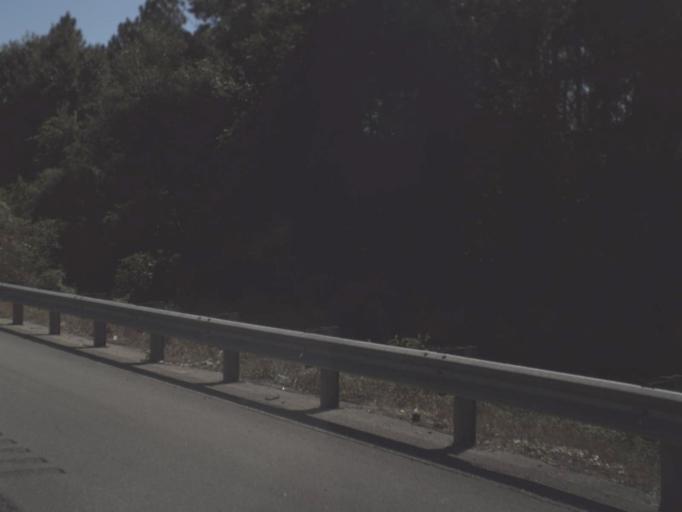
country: US
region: Florida
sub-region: Lake County
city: Howie In The Hills
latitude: 28.6444
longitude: -81.7931
